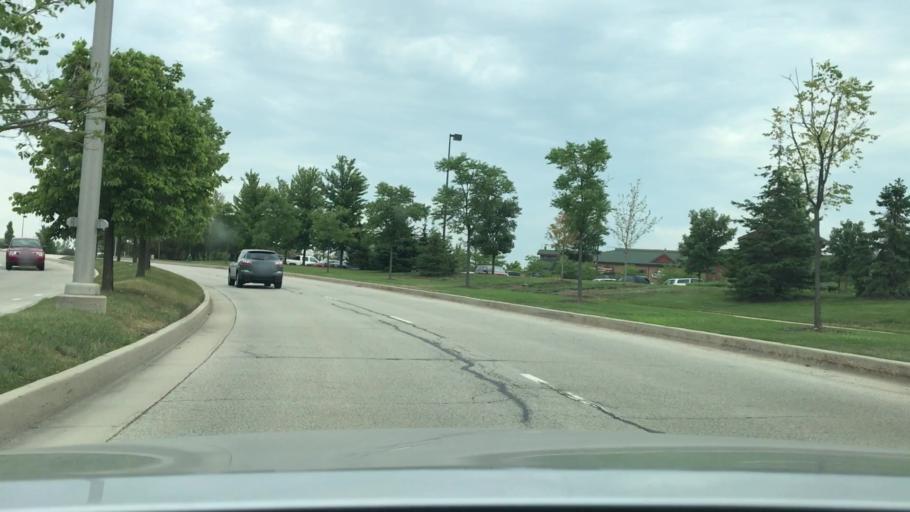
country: US
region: Illinois
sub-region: DuPage County
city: Woodridge
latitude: 41.7195
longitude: -88.0387
